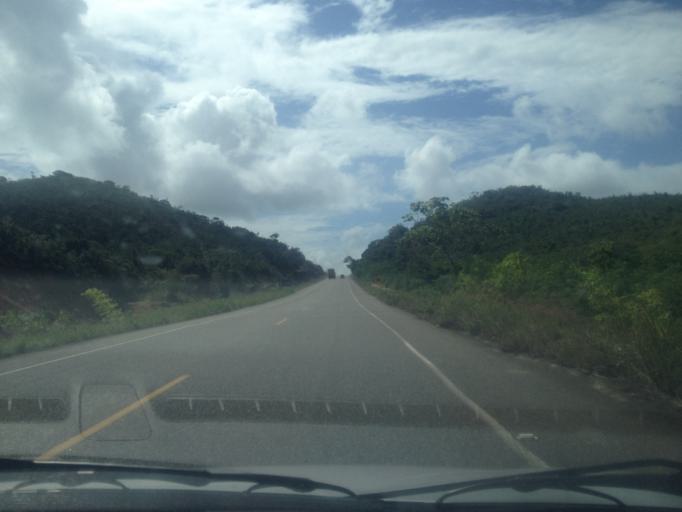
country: BR
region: Bahia
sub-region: Conde
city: Conde
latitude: -11.7272
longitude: -37.5786
